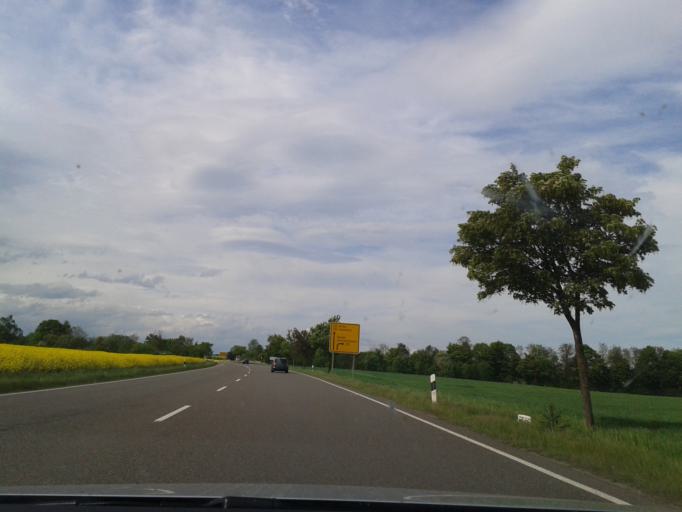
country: DE
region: Hesse
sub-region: Regierungsbezirk Kassel
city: Korbach
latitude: 51.2584
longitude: 8.9055
